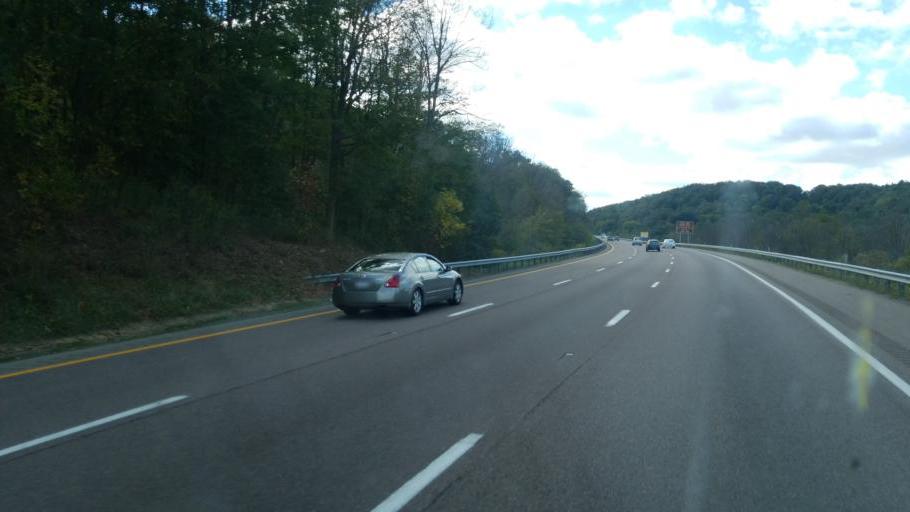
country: US
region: Maryland
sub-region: Allegany County
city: Frostburg
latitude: 39.6418
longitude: -78.8832
